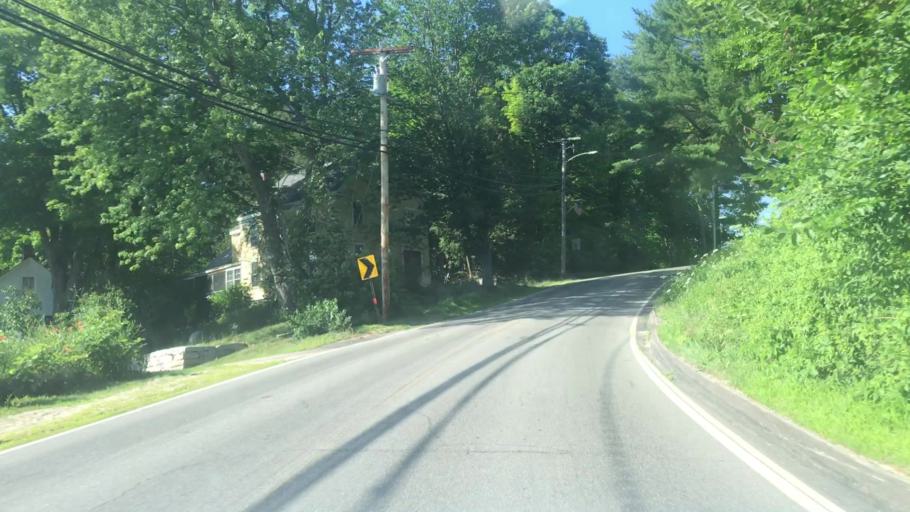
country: US
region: Maine
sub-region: York County
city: Hollis Center
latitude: 43.6673
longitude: -70.6018
